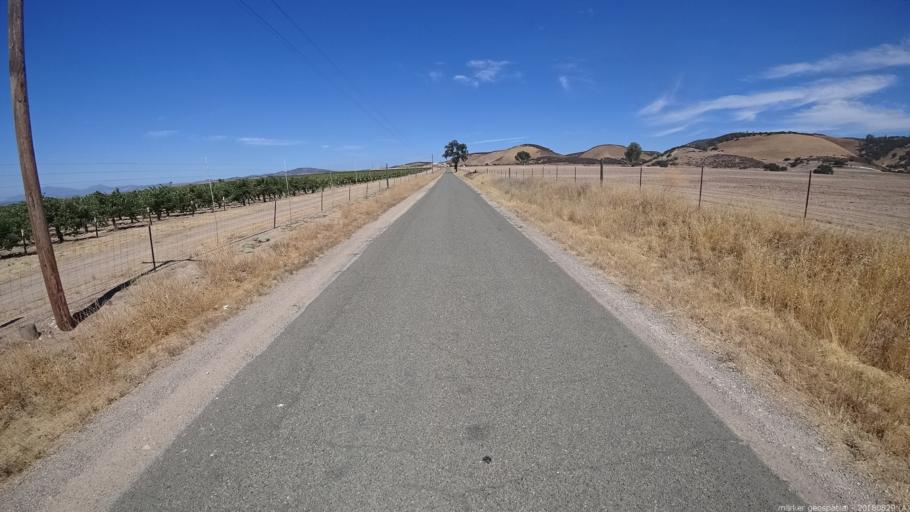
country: US
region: California
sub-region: San Luis Obispo County
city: Lake Nacimiento
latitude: 35.9187
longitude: -121.0379
